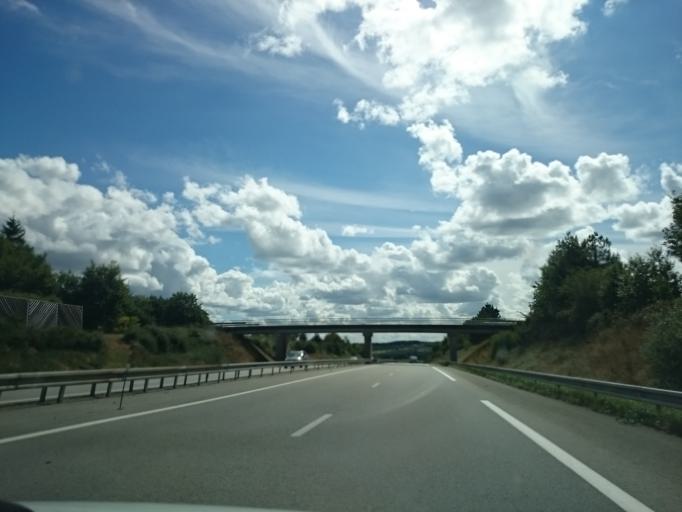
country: FR
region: Pays de la Loire
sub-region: Departement de la Loire-Atlantique
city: Mauves-sur-Loire
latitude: 47.3226
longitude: -1.4070
